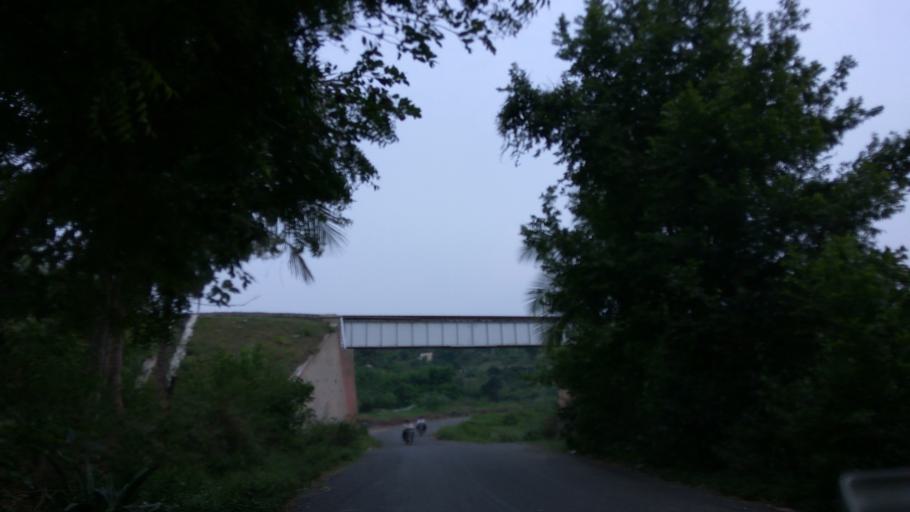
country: IN
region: Tamil Nadu
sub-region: Dharmapuri
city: Dharmapuri
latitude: 12.0214
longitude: 78.1174
